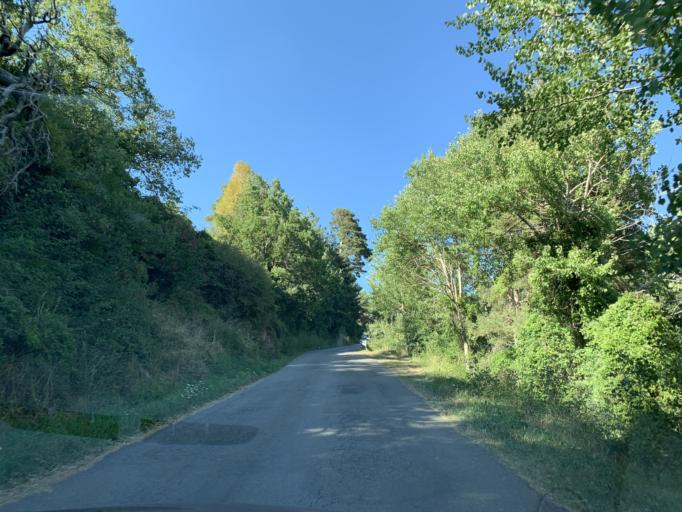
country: ES
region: Aragon
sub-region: Provincia de Huesca
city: Hoz de Jaca
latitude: 42.6940
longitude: -0.3319
